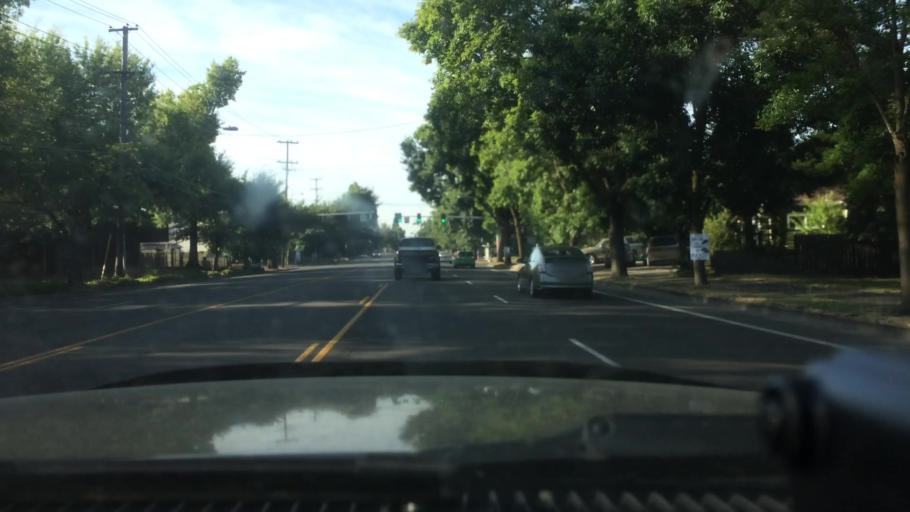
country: US
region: Oregon
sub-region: Lane County
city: Eugene
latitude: 44.0913
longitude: -123.1263
